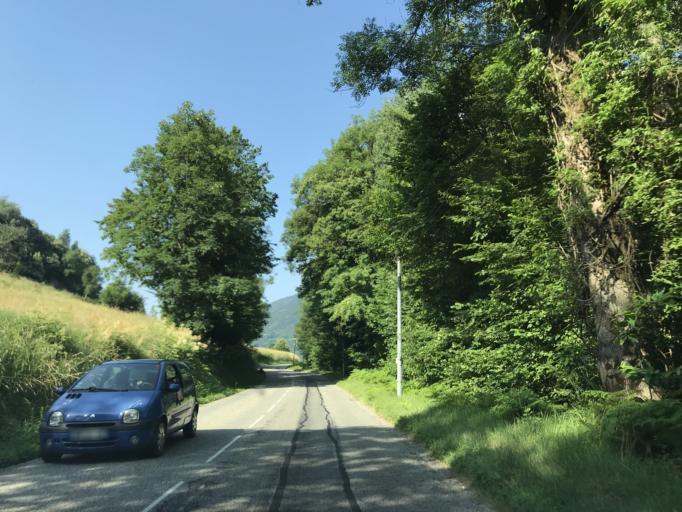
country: FR
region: Rhone-Alpes
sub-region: Departement de la Savoie
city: La Rochette
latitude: 45.4333
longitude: 6.1066
